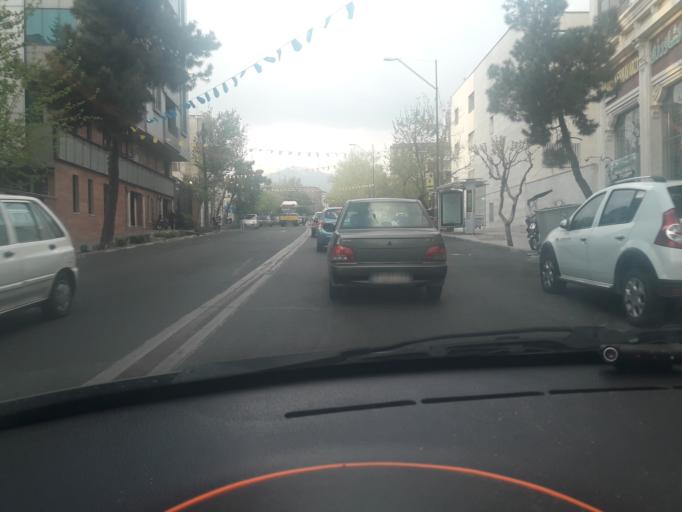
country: IR
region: Tehran
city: Tehran
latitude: 35.7451
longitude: 51.4049
